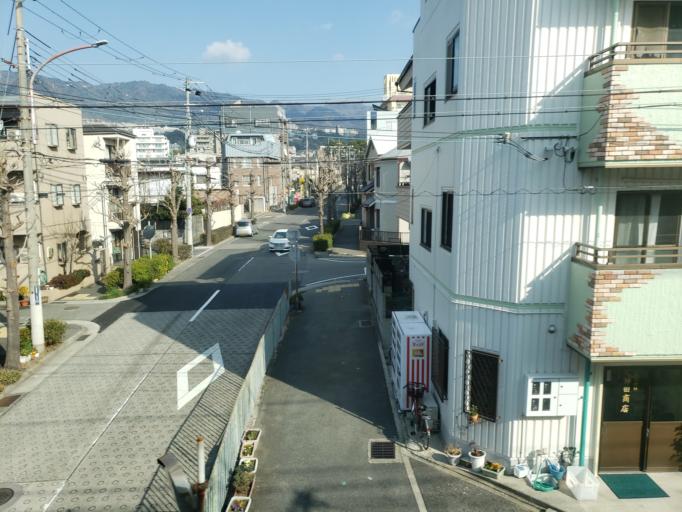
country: JP
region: Hyogo
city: Ashiya
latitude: 34.7192
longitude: 135.2570
